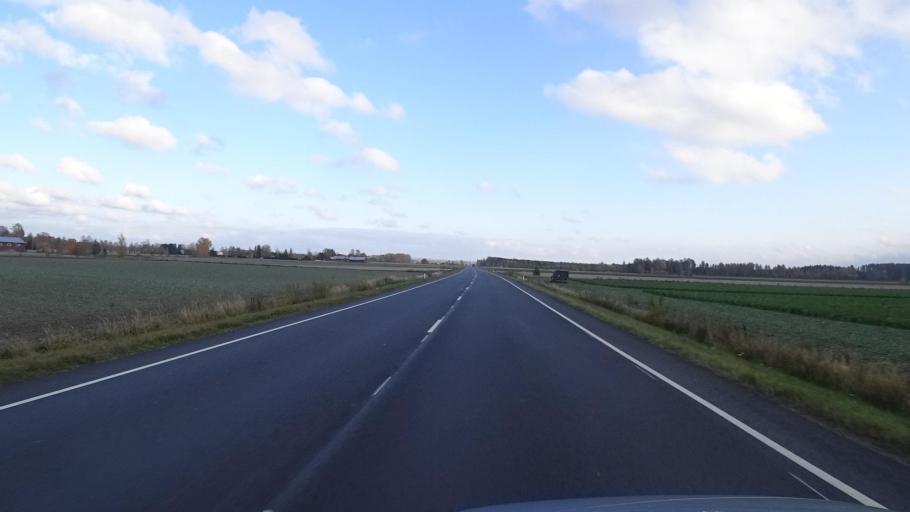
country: FI
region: Satakunta
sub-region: Rauma
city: Koeylioe
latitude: 61.0778
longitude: 22.2838
